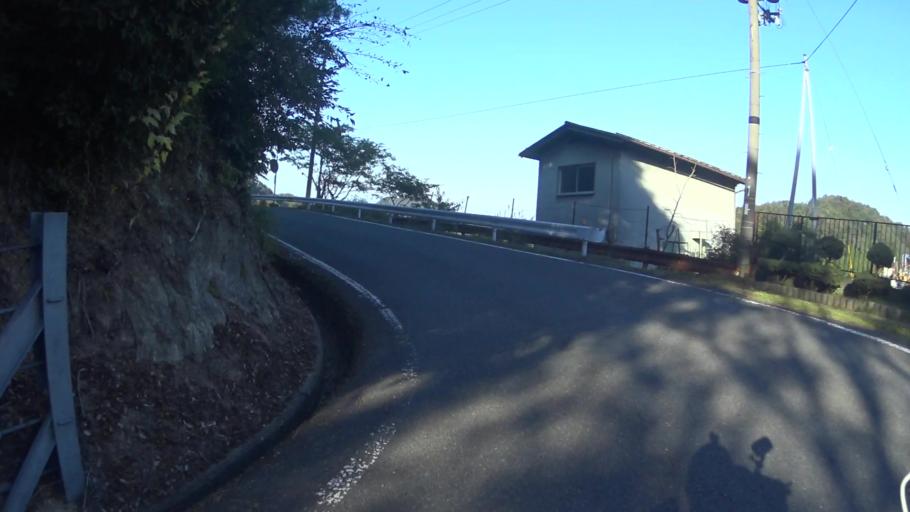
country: JP
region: Hyogo
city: Toyooka
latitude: 35.6159
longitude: 134.8734
